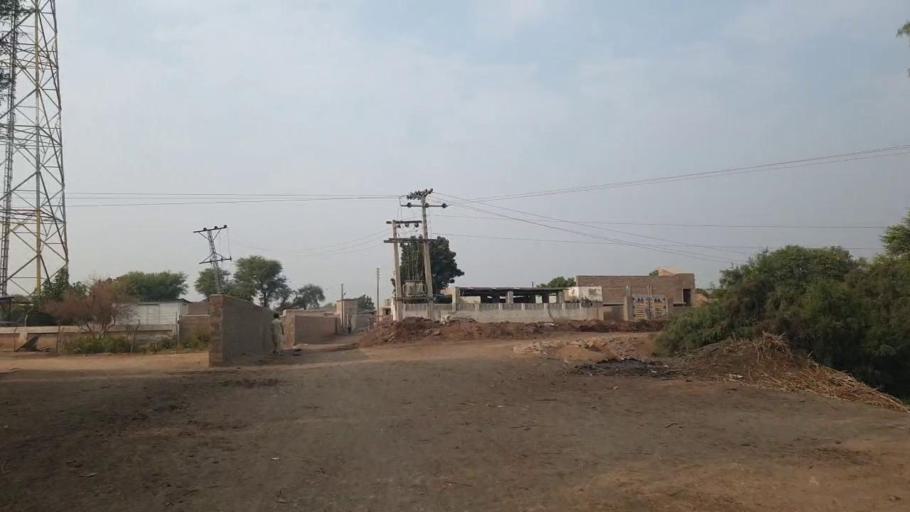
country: PK
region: Sindh
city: Sann
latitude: 26.1271
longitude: 68.0642
